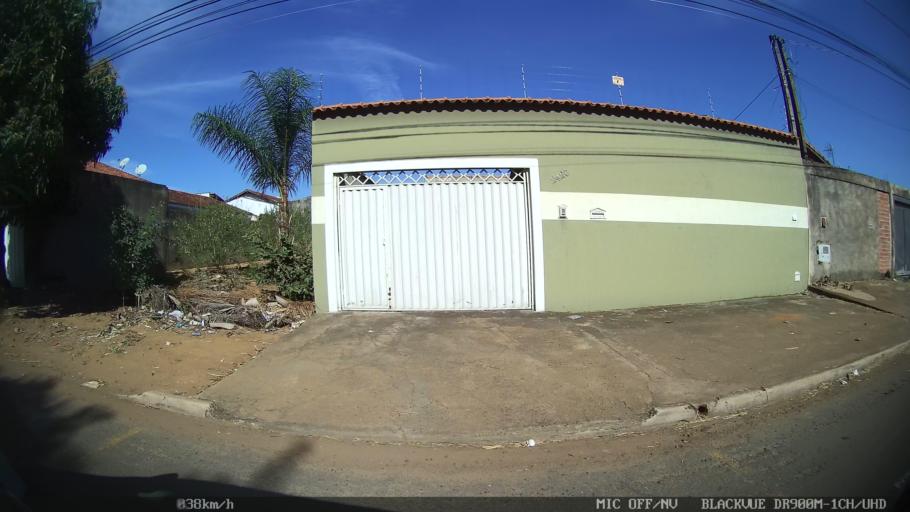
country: BR
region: Sao Paulo
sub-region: Franca
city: Franca
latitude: -20.5073
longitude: -47.4208
